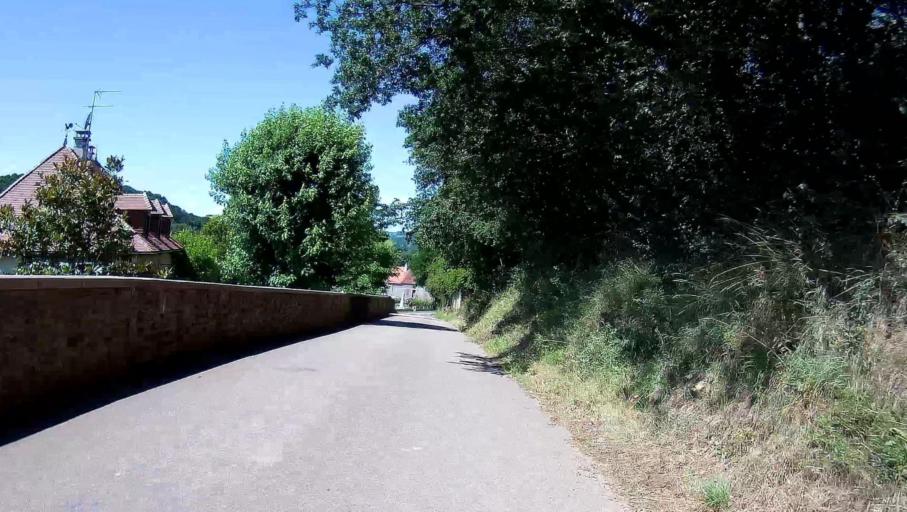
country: FR
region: Bourgogne
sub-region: Departement de Saone-et-Loire
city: Saint-Leger-sur-Dheune
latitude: 46.8676
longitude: 4.6289
